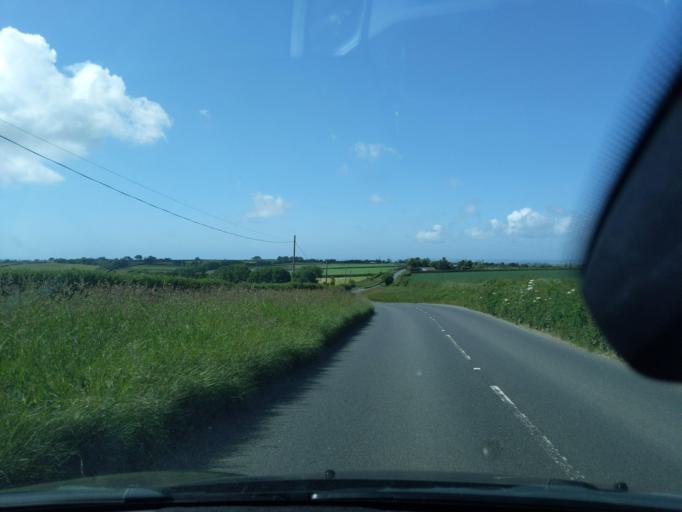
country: GB
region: England
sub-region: Devon
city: Great Torrington
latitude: 50.9937
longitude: -4.0957
